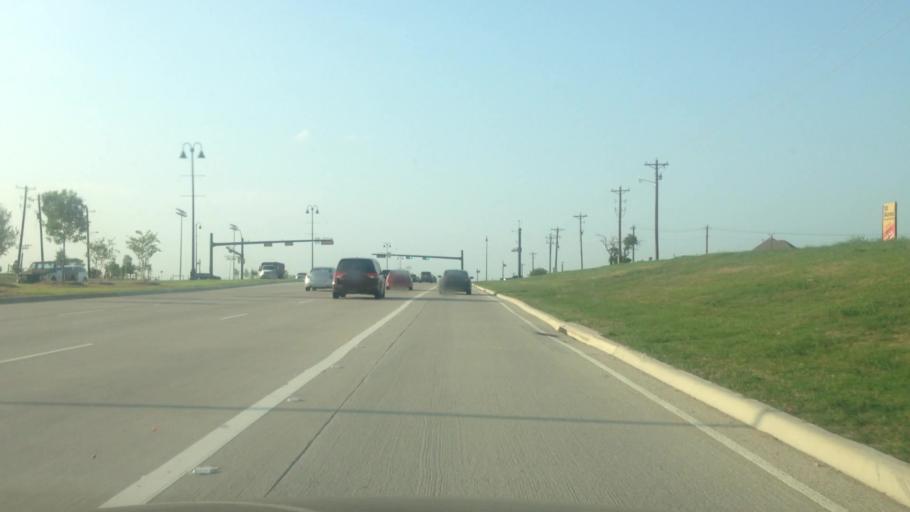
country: US
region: Texas
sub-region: Denton County
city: The Colony
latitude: 33.1125
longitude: -96.8917
